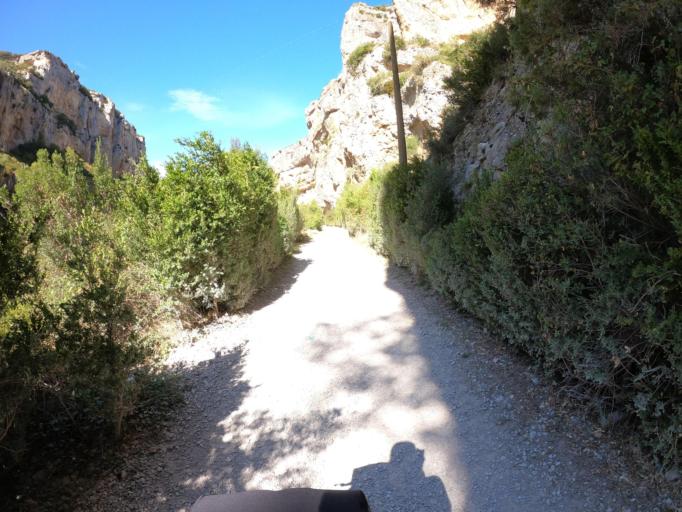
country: ES
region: Navarre
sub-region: Provincia de Navarra
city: Lumbier
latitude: 42.6311
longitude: -1.3005
